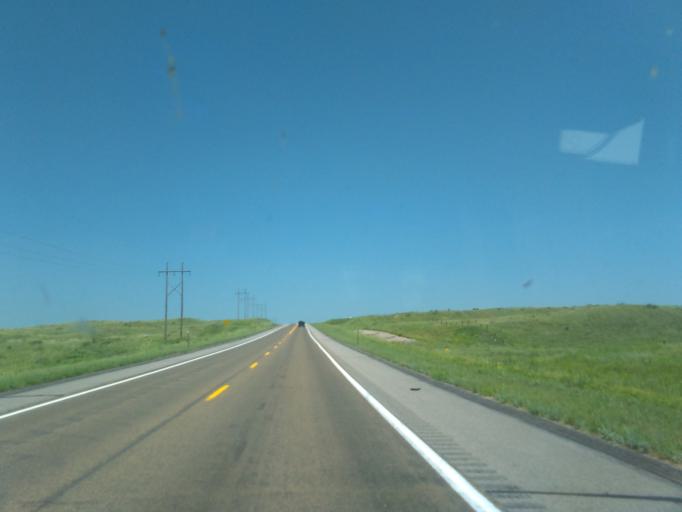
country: US
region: Nebraska
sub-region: Lincoln County
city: North Platte
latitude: 40.8696
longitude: -100.7540
